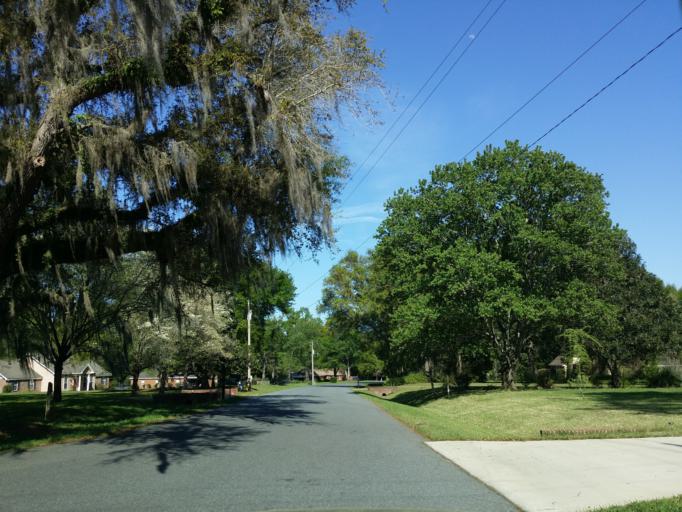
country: US
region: Florida
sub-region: Leon County
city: Tallahassee
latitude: 30.4811
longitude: -84.1941
